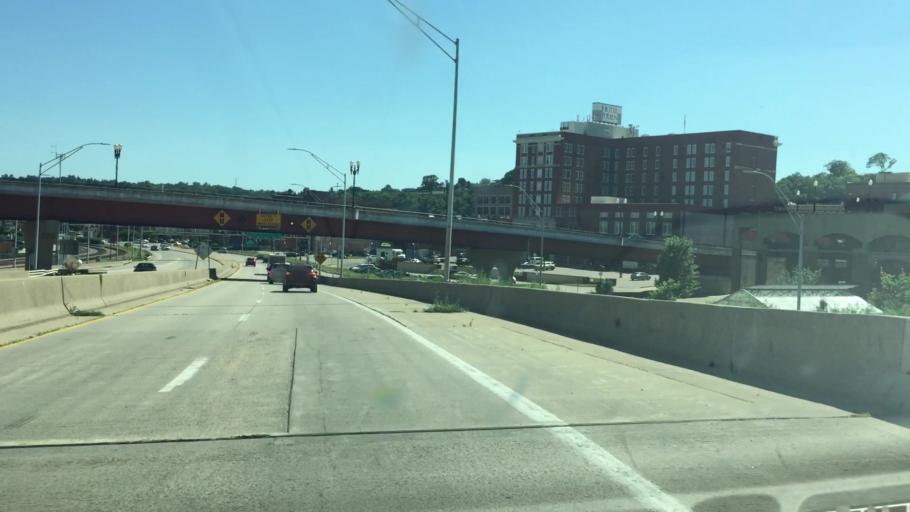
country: US
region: Iowa
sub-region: Dubuque County
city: Dubuque
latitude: 42.4981
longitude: -90.6631
